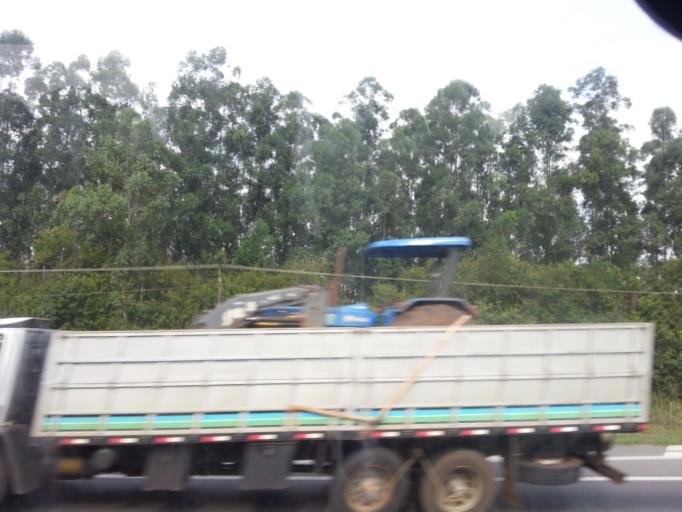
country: BR
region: Sao Paulo
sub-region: Jacarei
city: Jacarei
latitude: -23.2676
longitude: -45.9627
